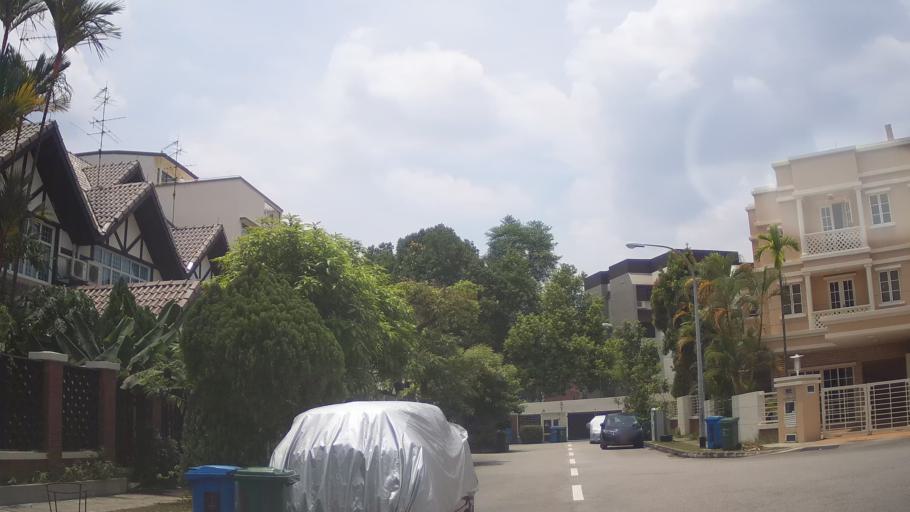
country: MY
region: Johor
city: Johor Bahru
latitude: 1.3701
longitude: 103.7688
